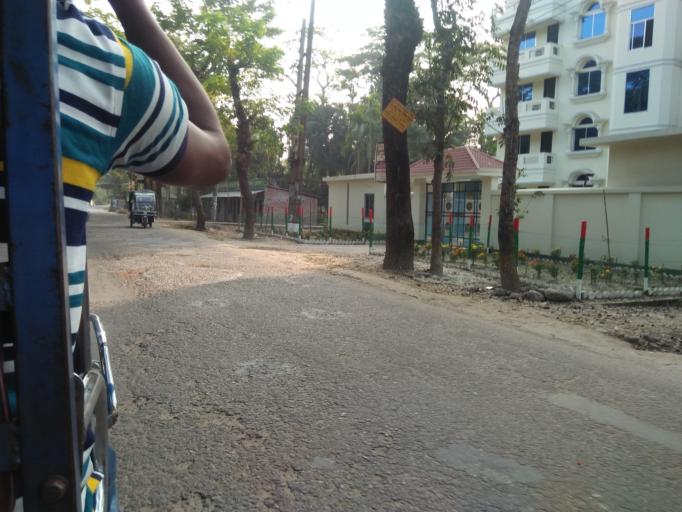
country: BD
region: Barisal
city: Bhola
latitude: 22.6959
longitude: 90.6435
